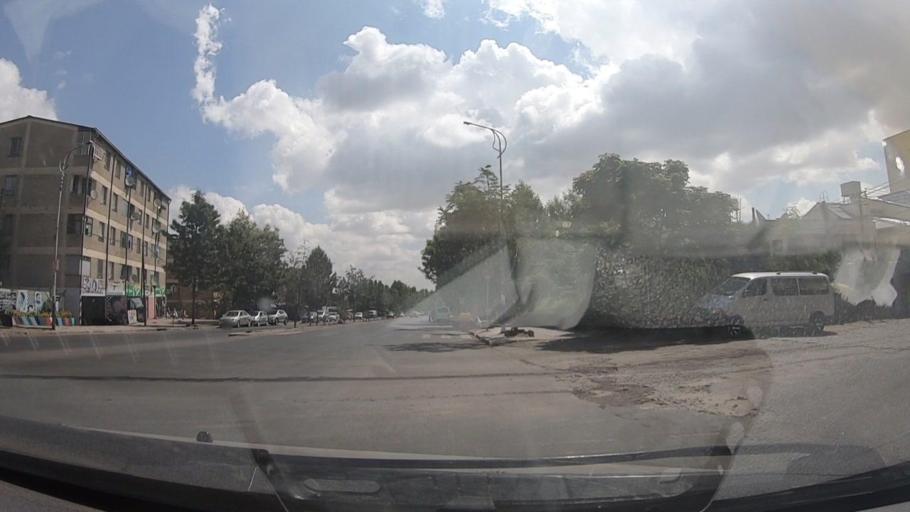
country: ET
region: Adis Abeba
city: Addis Ababa
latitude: 8.9757
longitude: 38.7232
